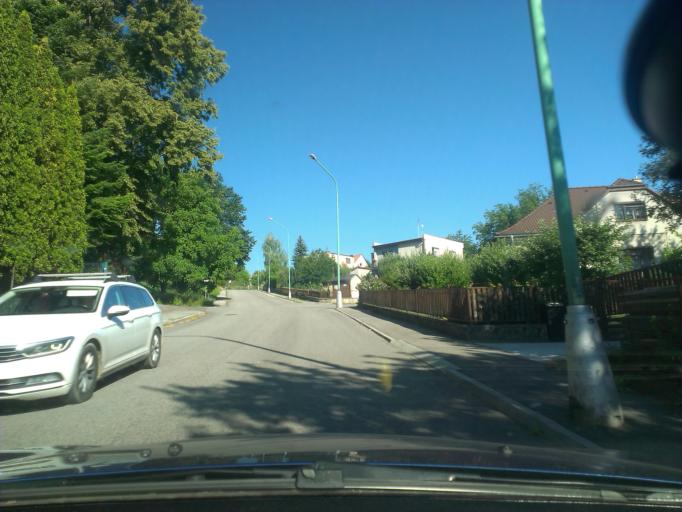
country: SK
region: Trenciansky
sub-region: Okres Myjava
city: Myjava
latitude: 48.7581
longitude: 17.5647
